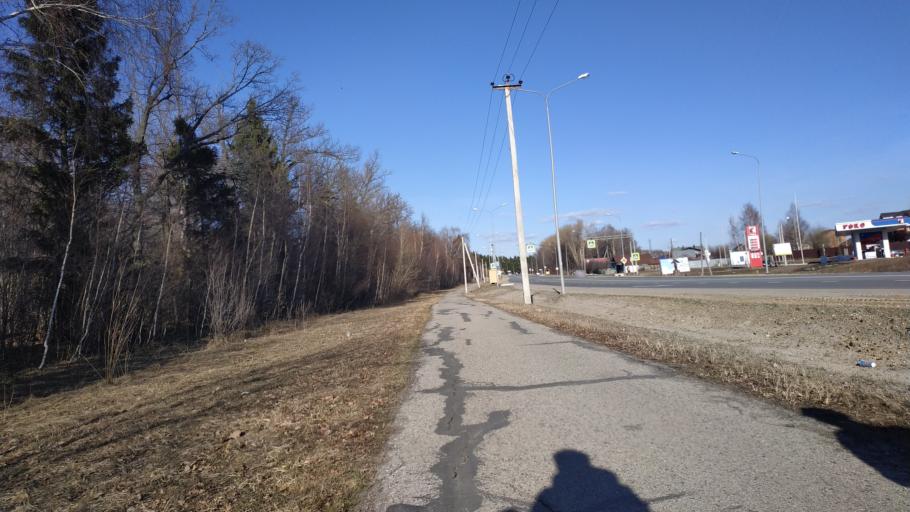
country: RU
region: Chuvashia
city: Ishley
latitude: 56.1335
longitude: 47.0838
